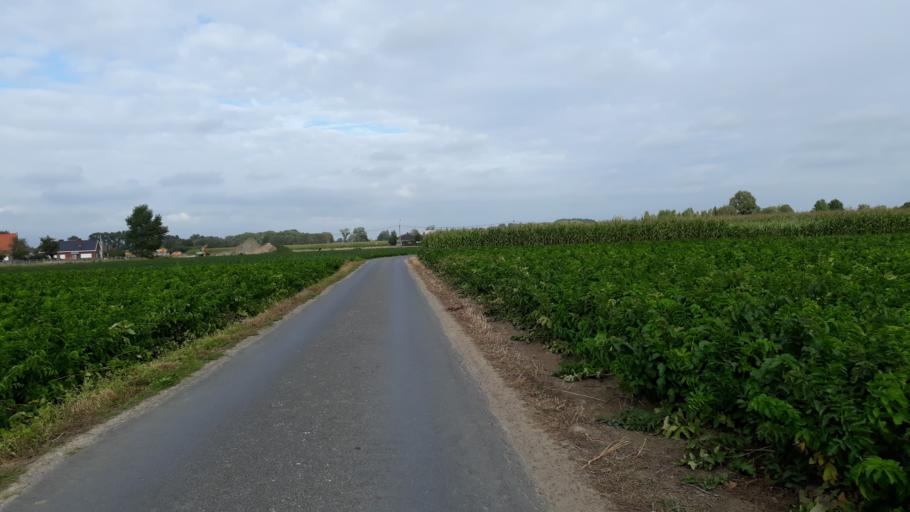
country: BE
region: Flanders
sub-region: Provincie West-Vlaanderen
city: Torhout
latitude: 51.0500
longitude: 3.1224
